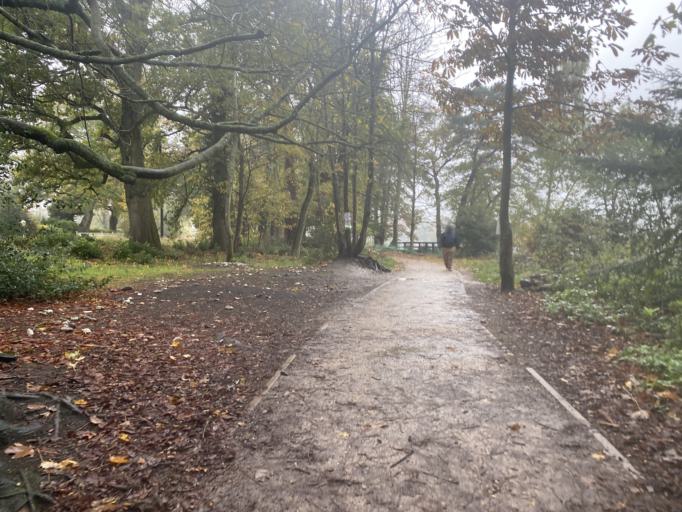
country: GB
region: England
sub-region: Hampshire
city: Petersfield
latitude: 50.9983
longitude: -0.9271
